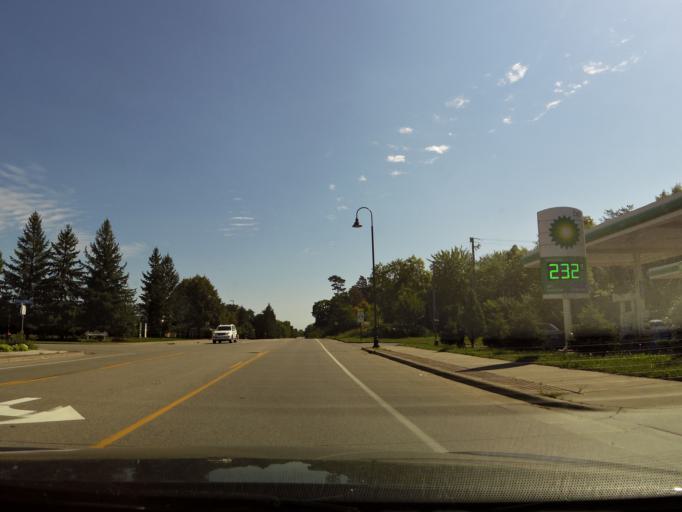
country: US
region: Minnesota
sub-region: Hennepin County
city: Deephaven
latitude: 44.9420
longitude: -93.5004
